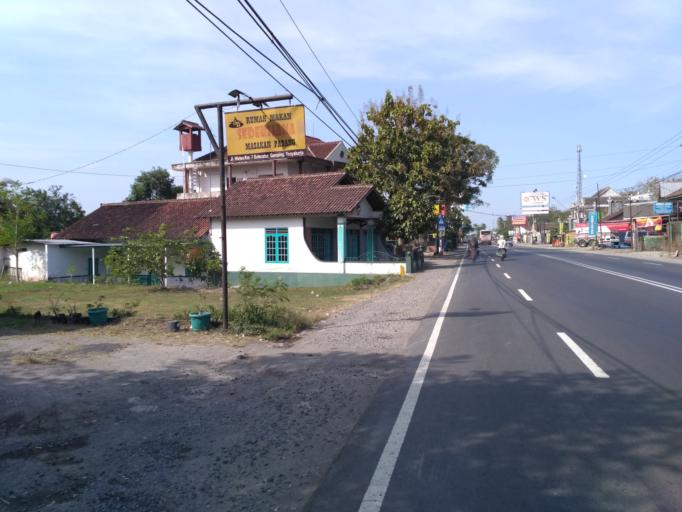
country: ID
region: Daerah Istimewa Yogyakarta
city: Godean
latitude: -7.8087
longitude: 110.2870
